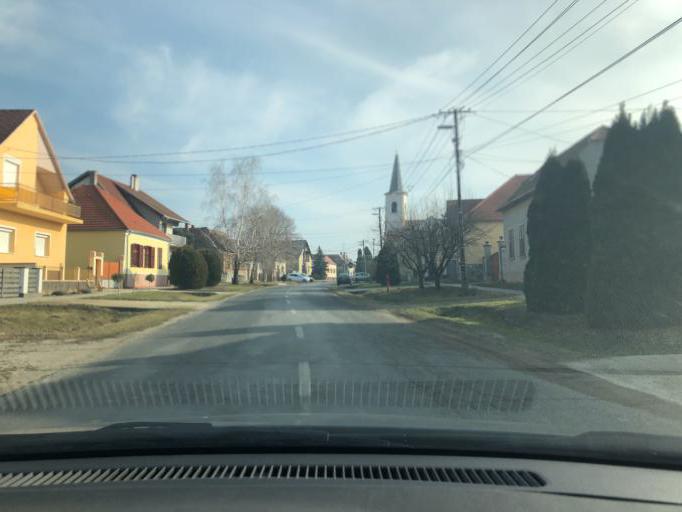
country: HU
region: Gyor-Moson-Sopron
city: Kapuvar
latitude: 47.5994
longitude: 17.0864
